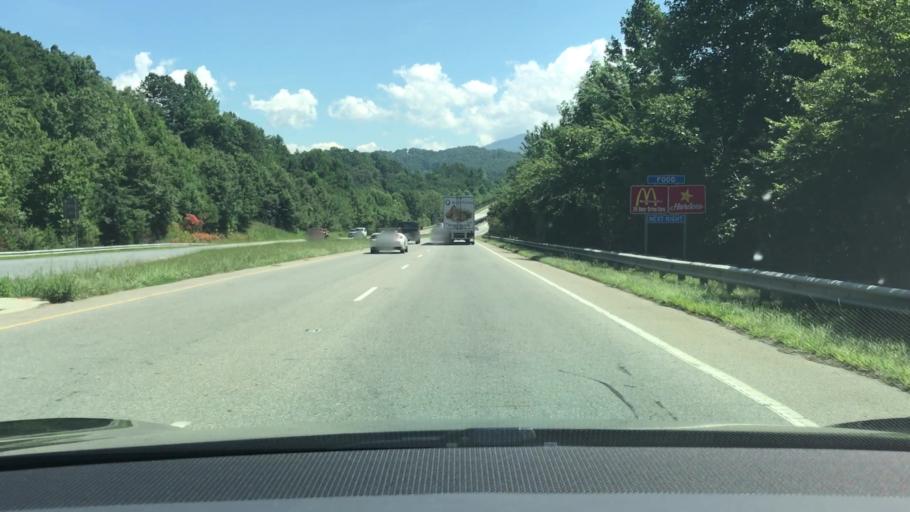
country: US
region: North Carolina
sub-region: Macon County
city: Franklin
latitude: 35.1674
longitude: -83.3689
